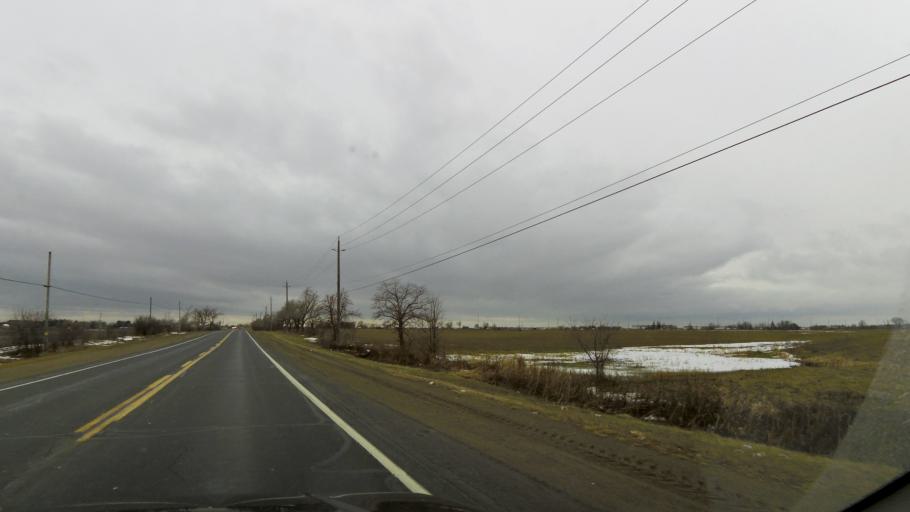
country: CA
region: Ontario
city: Brampton
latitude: 43.8381
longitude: -79.6816
